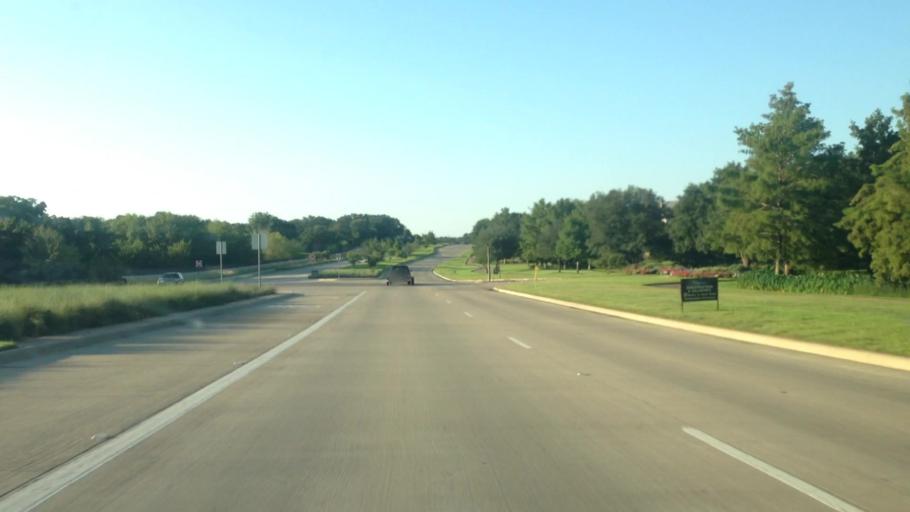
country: US
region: Texas
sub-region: Denton County
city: Trophy Club
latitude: 32.9717
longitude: -97.1862
